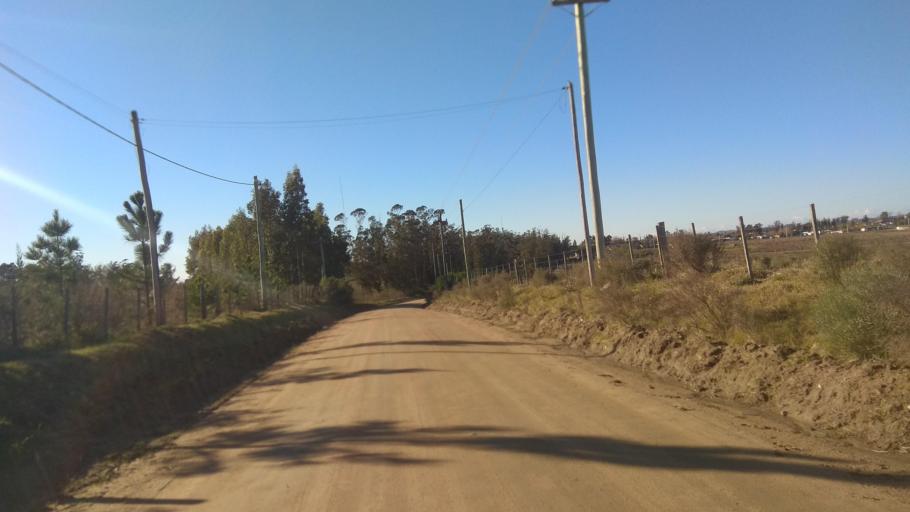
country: UY
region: Florida
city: Florida
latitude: -34.0930
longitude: -56.2468
